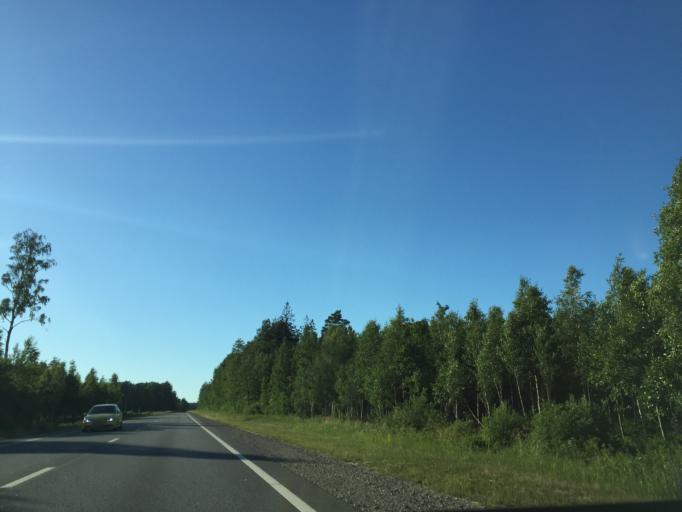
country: LV
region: Ventspils
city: Ventspils
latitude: 57.3834
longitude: 21.7098
